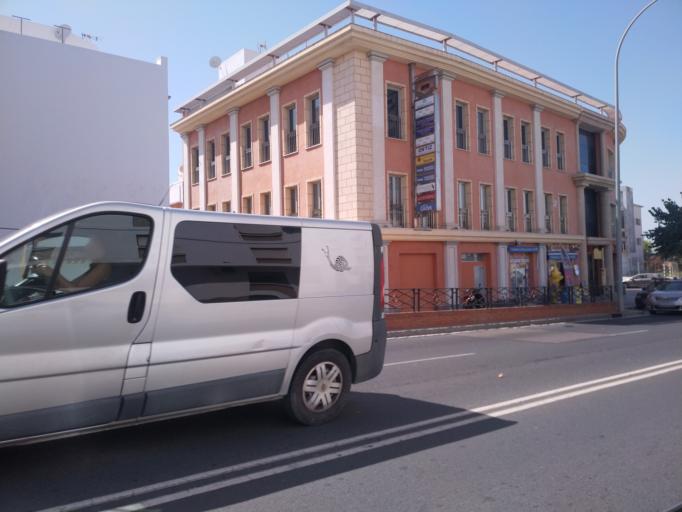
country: ES
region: Andalusia
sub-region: Provincia de Cadiz
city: Chiclana de la Frontera
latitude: 36.4195
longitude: -6.1568
